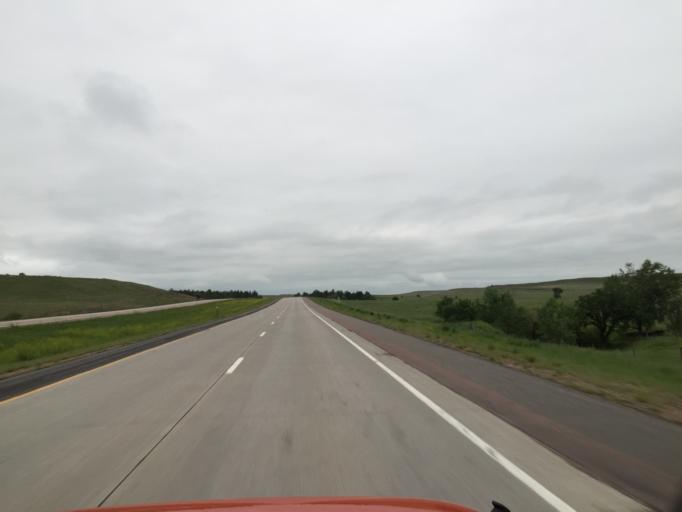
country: US
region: South Dakota
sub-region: Fall River County
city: Hot Springs
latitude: 43.4394
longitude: -103.3676
